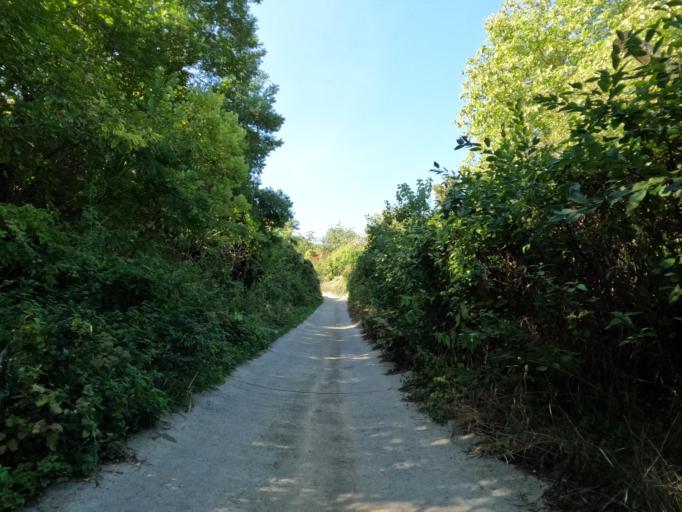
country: HU
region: Tolna
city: Szekszard
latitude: 46.3506
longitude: 18.6730
